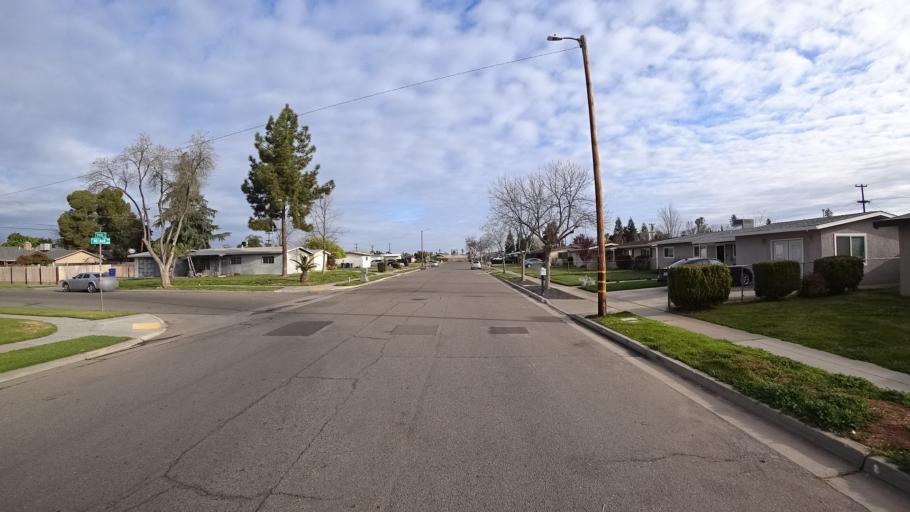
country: US
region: California
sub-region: Fresno County
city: Fresno
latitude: 36.8318
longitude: -119.7943
